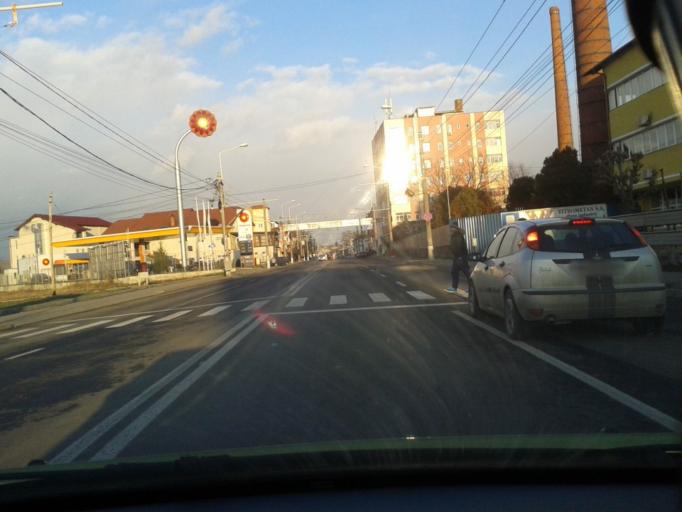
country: RO
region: Sibiu
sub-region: Municipiul Medias
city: Medias
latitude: 46.1535
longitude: 24.3363
